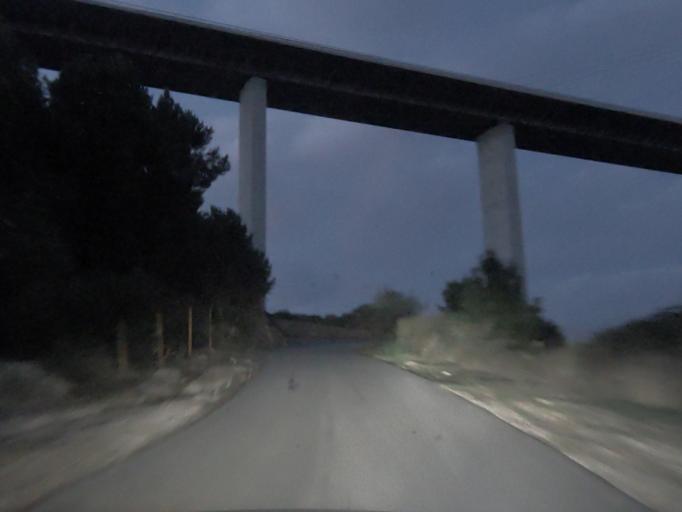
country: PT
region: Vila Real
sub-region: Vila Real
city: Vila Real
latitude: 41.2773
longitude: -7.7552
